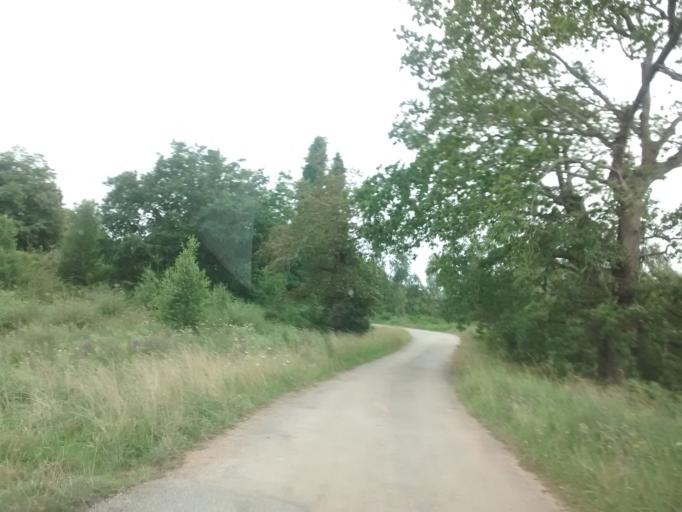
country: ES
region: Cantabria
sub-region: Provincia de Cantabria
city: Comillas
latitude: 43.3427
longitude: -4.2938
